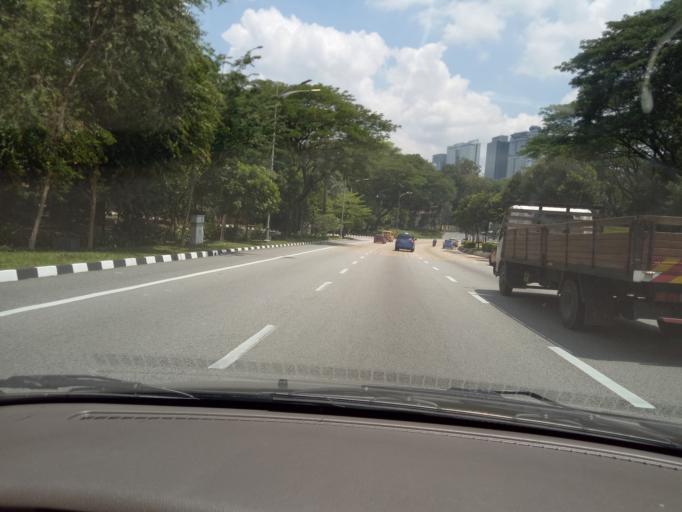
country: MY
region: Kuala Lumpur
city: Kuala Lumpur
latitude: 3.1322
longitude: 101.6998
